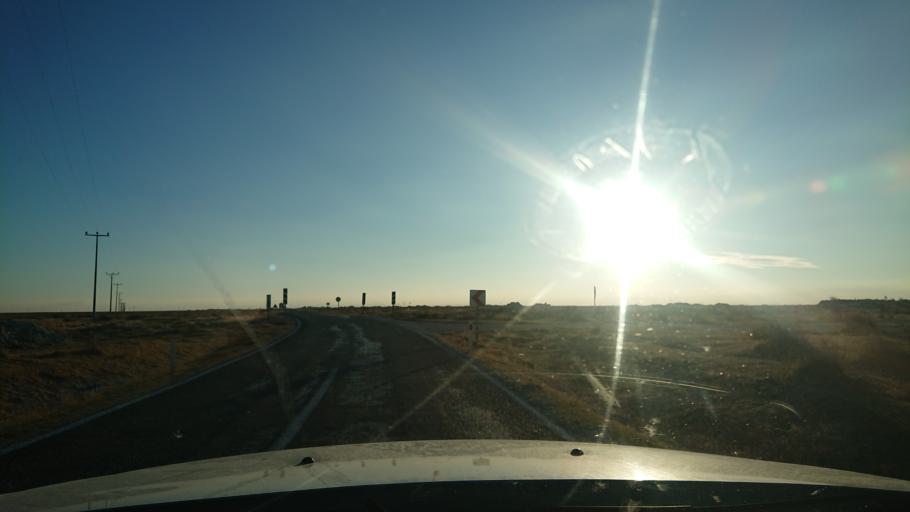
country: TR
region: Aksaray
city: Eskil
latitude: 38.5266
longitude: 33.2065
